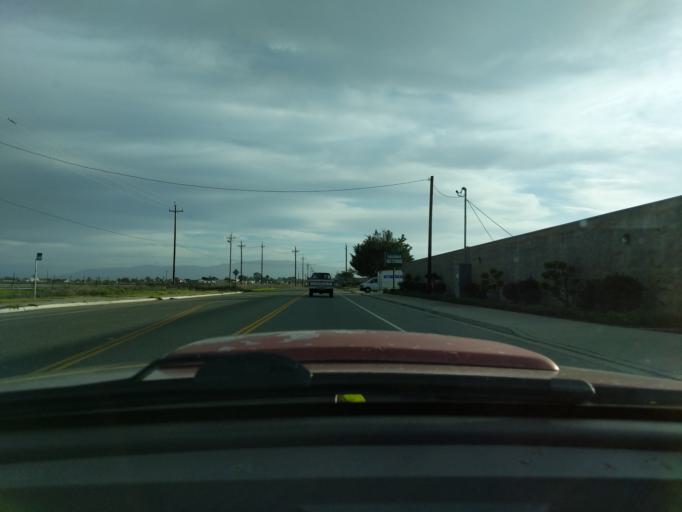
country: US
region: California
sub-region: Monterey County
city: Prunedale
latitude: 36.7435
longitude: -121.6570
